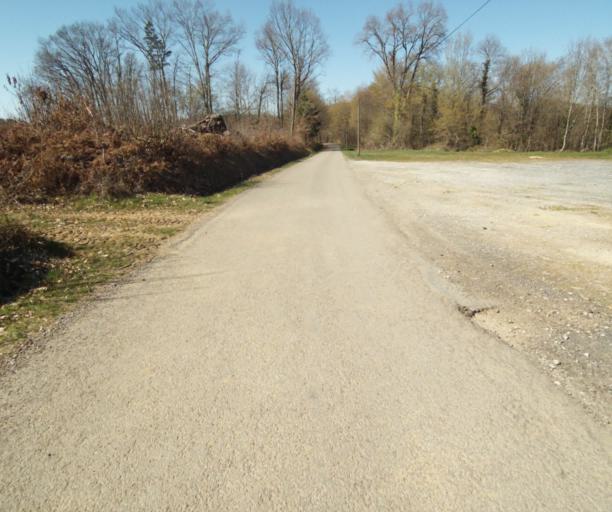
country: FR
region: Limousin
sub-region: Departement de la Correze
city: Chameyrat
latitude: 45.2514
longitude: 1.7110
